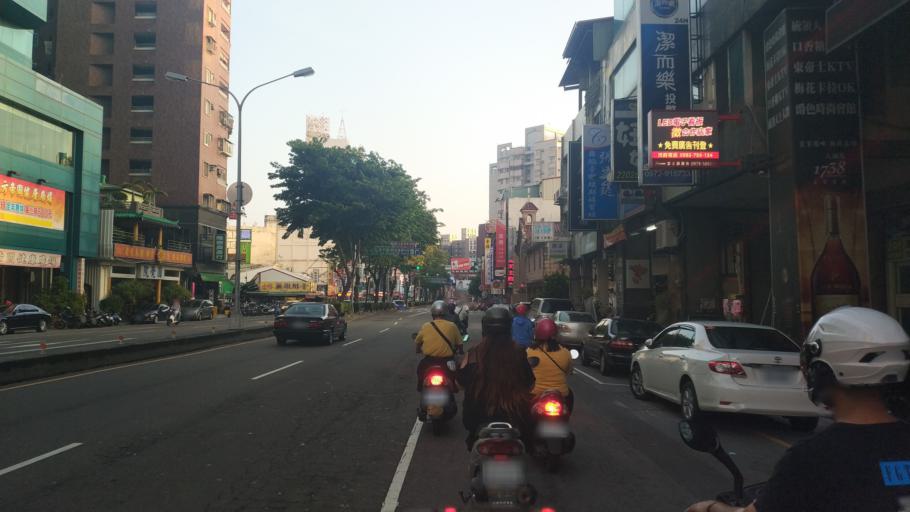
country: TW
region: Taiwan
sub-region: Taichung City
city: Taichung
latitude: 24.1537
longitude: 120.6773
